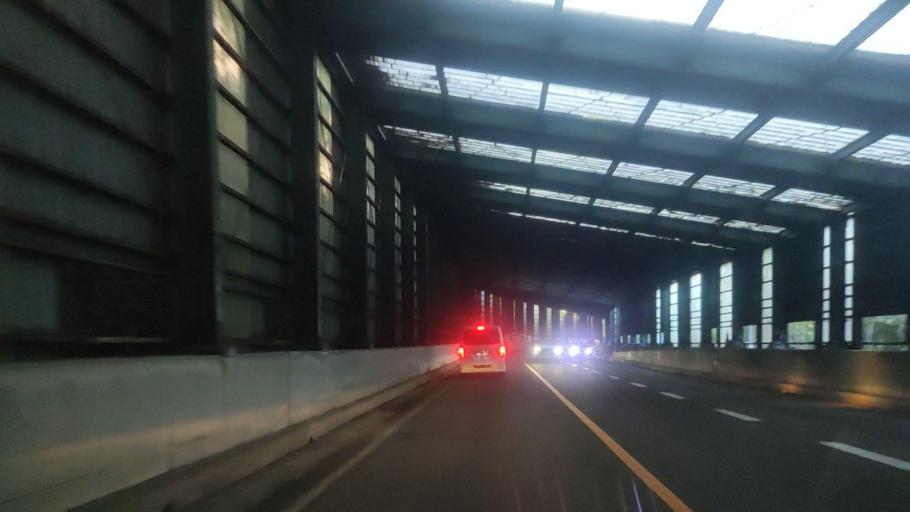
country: JP
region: Nagano
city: Kamimaruko
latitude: 36.1783
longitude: 138.2823
